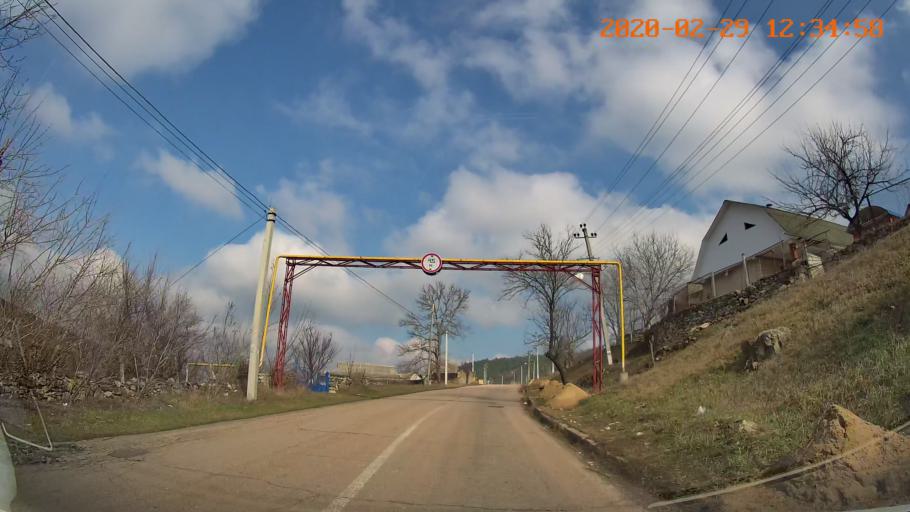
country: MD
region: Telenesti
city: Camenca
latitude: 48.0438
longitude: 28.7175
